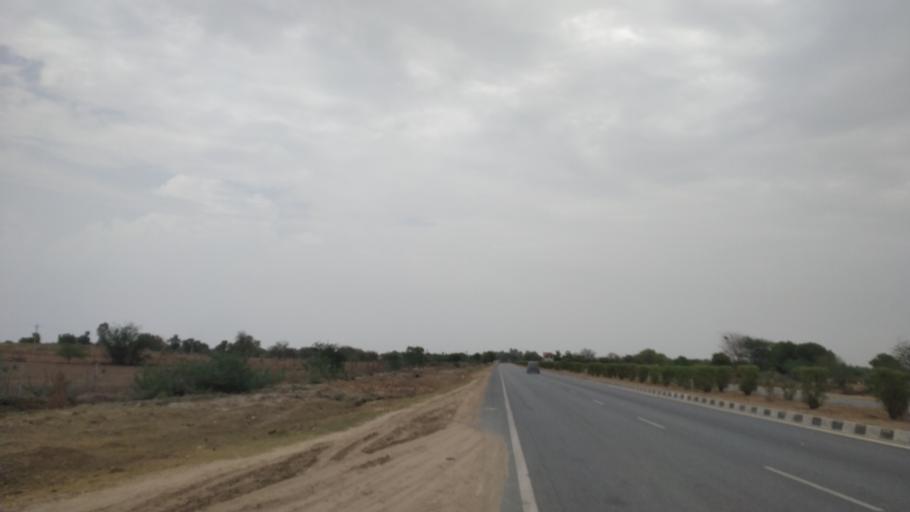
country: IN
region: Rajasthan
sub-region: Tonk
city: Todaraisingh
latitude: 25.9601
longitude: 75.6449
